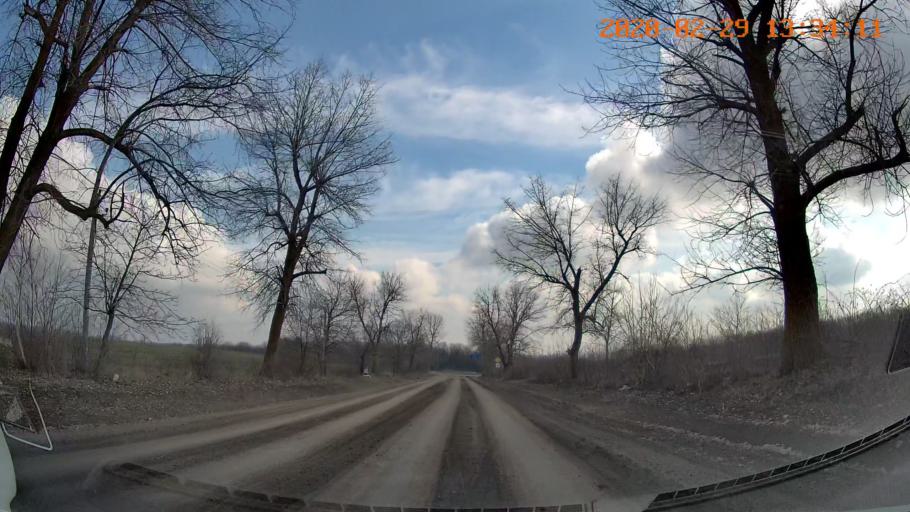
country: MD
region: Telenesti
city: Camenca
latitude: 47.8702
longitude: 28.6210
